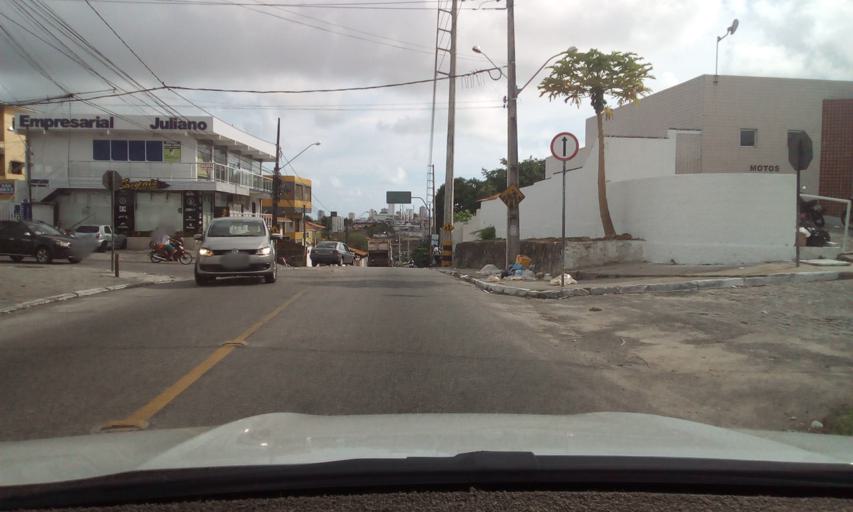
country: BR
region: Paraiba
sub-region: Joao Pessoa
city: Joao Pessoa
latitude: -7.1073
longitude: -34.8686
